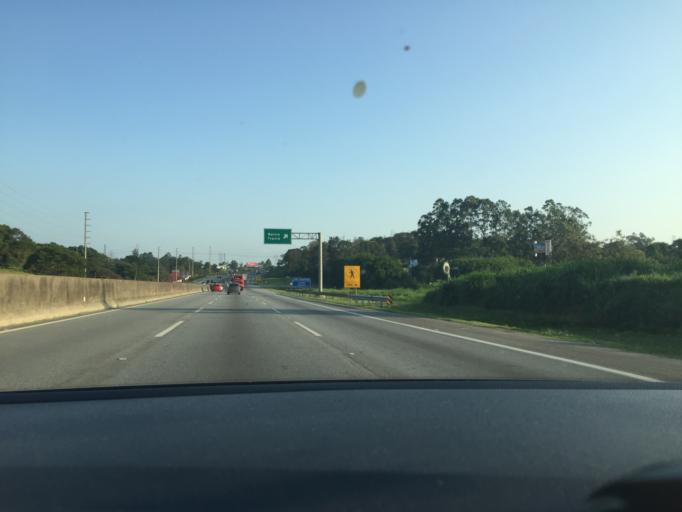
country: BR
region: Sao Paulo
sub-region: Louveira
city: Louveira
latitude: -23.1098
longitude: -46.9600
